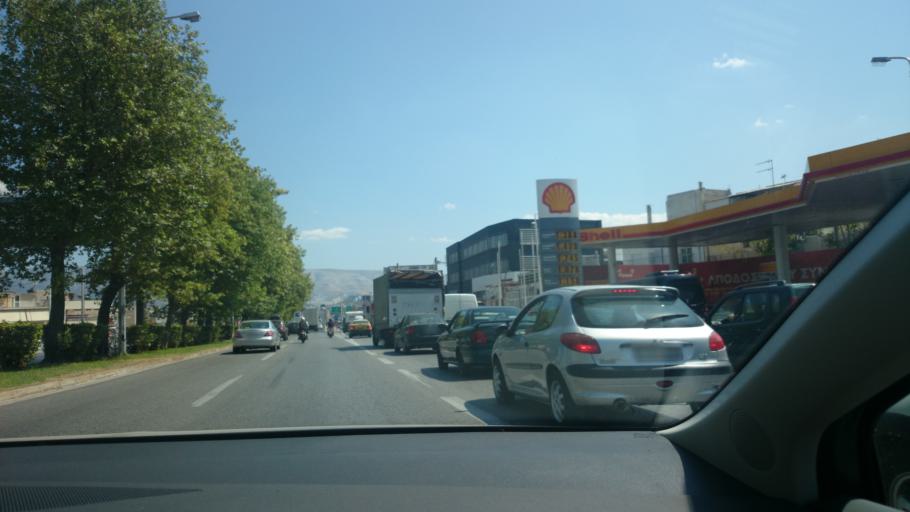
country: GR
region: Attica
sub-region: Nomarchia Athinas
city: Peristeri
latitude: 37.9987
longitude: 23.6906
